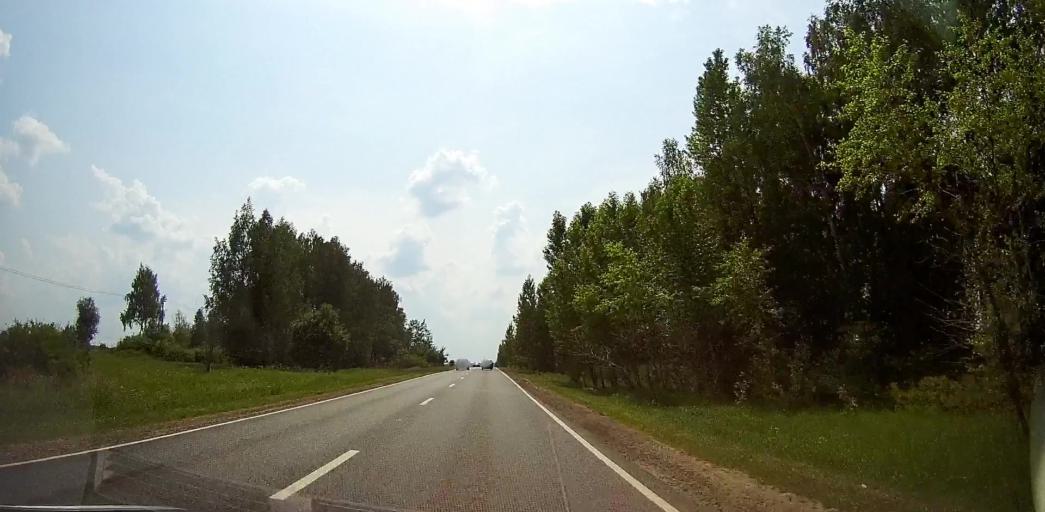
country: RU
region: Moskovskaya
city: Malino
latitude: 55.0787
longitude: 38.1647
